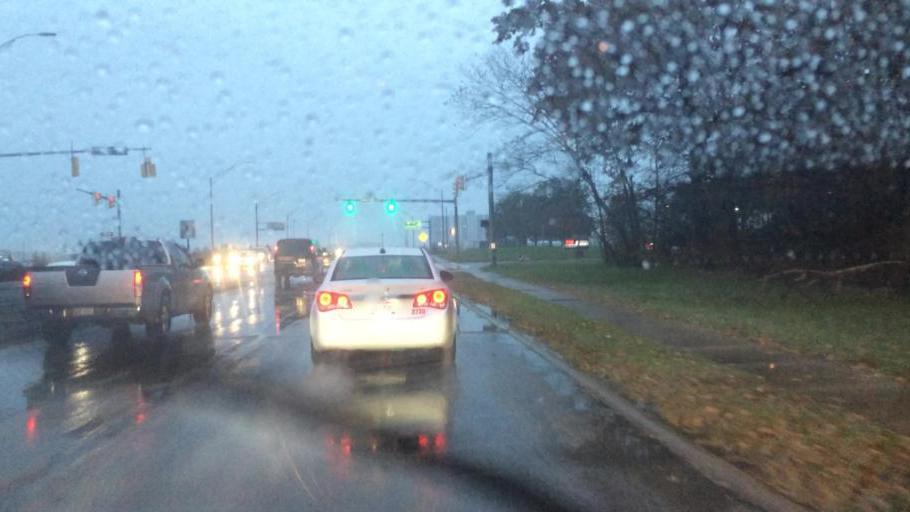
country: US
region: Ohio
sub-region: Cuyahoga County
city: North Olmsted
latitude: 41.4102
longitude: -81.9020
